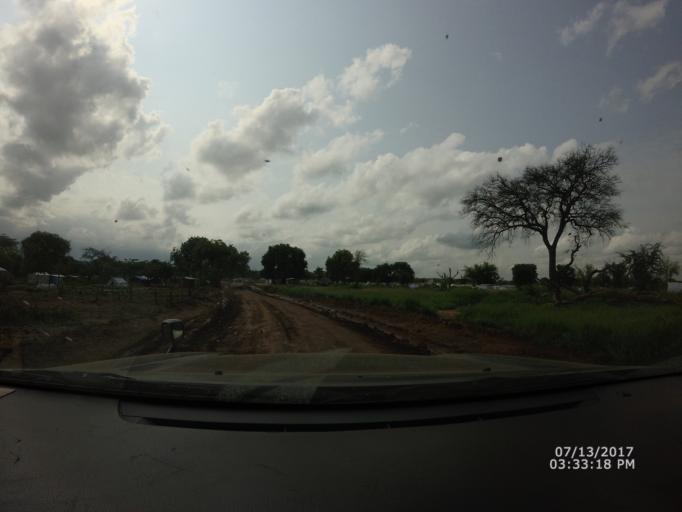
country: UG
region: Northern Region
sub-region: Yumbe District
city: Yumbe
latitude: 3.2250
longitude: 31.2817
